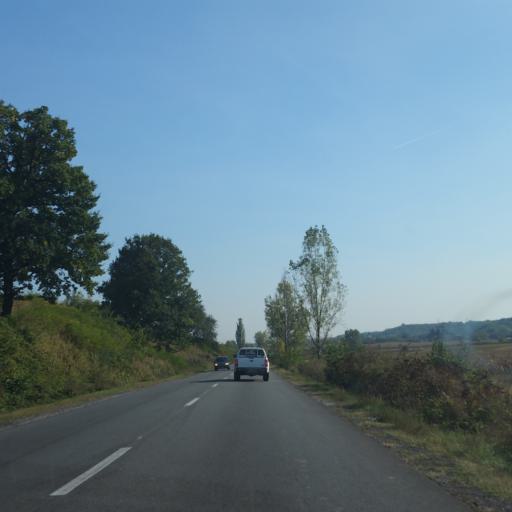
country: RO
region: Arges
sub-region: Comuna Merisani
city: Merisani
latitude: 44.9578
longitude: 24.7563
